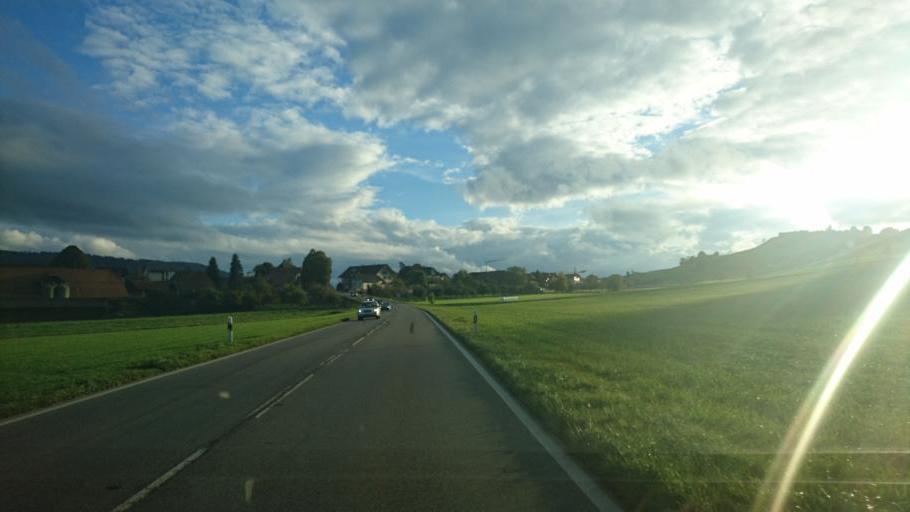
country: CH
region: Bern
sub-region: Bern-Mittelland District
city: Konolfingen
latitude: 46.8941
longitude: 7.6333
